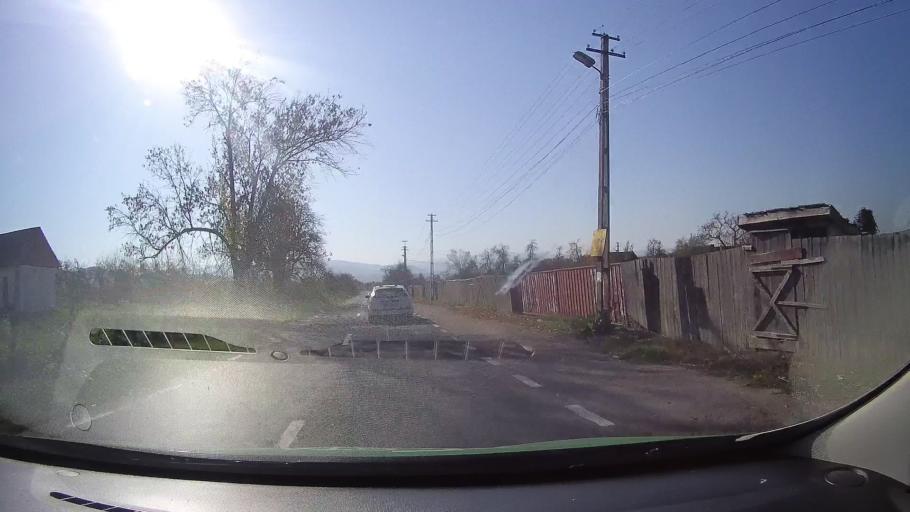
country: RO
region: Timis
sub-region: Comuna Curtea
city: Curtea
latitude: 45.8482
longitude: 22.3133
